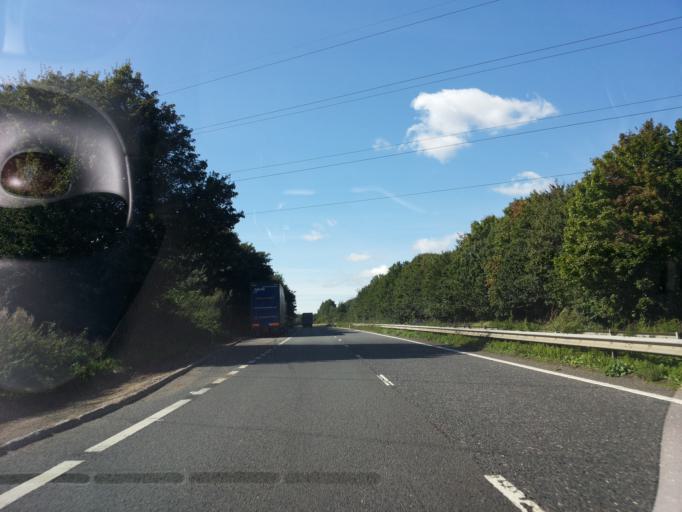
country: GB
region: England
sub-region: Kent
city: Canterbury
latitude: 51.2552
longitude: 1.1007
